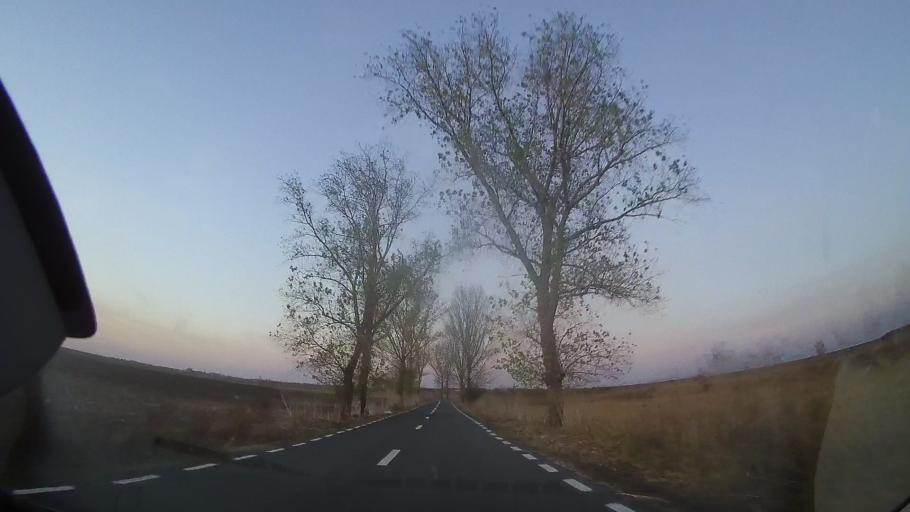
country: RO
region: Constanta
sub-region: Comuna Cobadin
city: Cobadin
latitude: 44.0383
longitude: 28.2580
